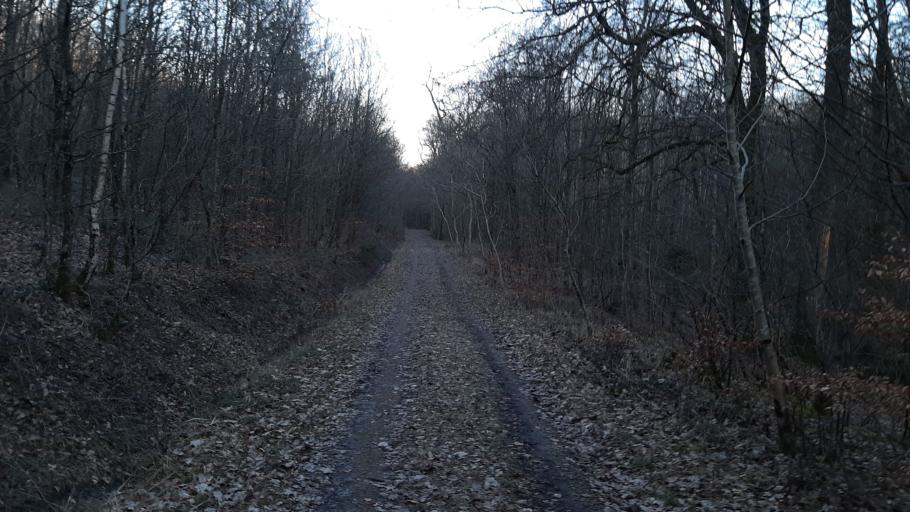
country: LU
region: Grevenmacher
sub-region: Canton d'Echternach
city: Mompach
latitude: 49.7391
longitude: 6.4836
